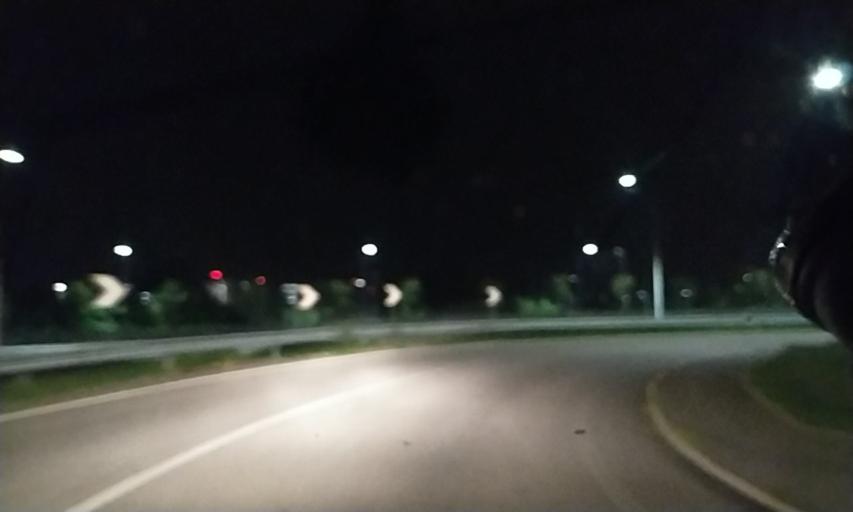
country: IT
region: Piedmont
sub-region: Provincia di Biella
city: Ponderano
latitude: 45.5476
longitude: 8.0600
